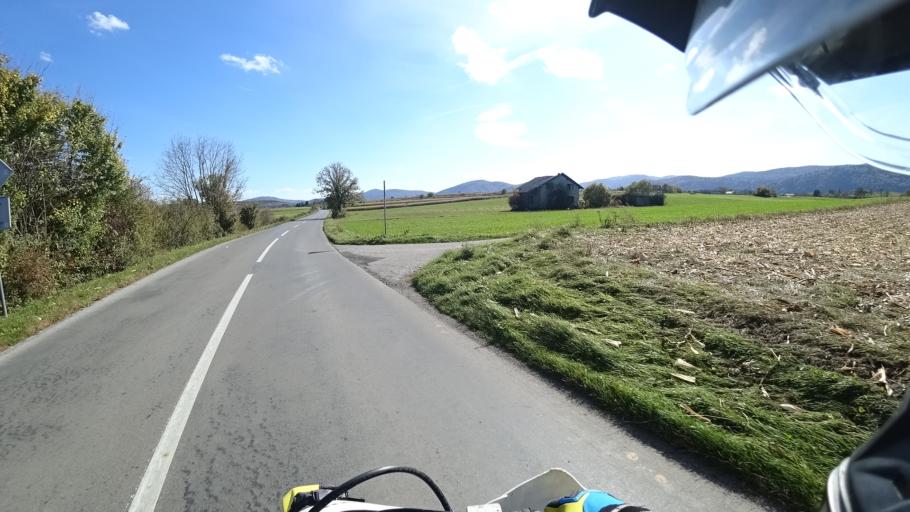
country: HR
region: Karlovacka
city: Plaski
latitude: 45.0947
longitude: 15.3533
